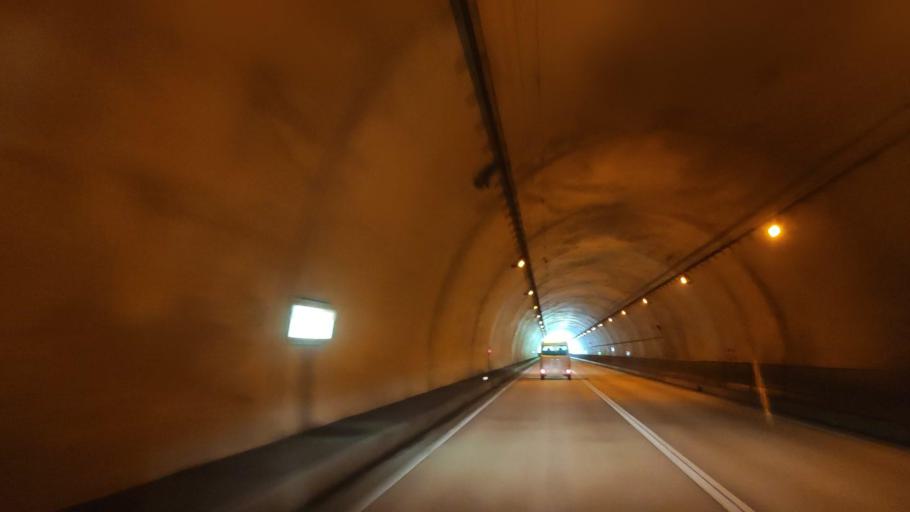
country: JP
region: Hyogo
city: Toyooka
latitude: 35.4916
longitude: 134.6206
